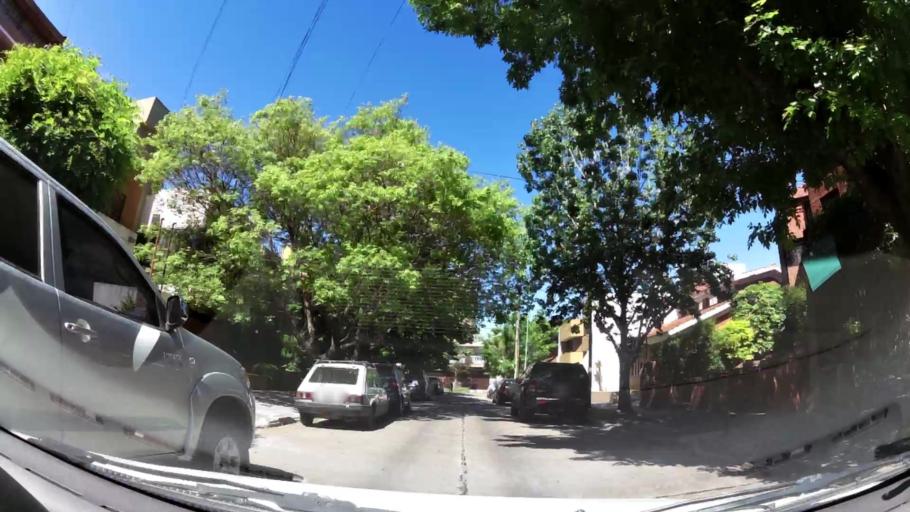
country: AR
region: Buenos Aires
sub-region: Partido de Vicente Lopez
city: Olivos
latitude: -34.5252
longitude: -58.4986
